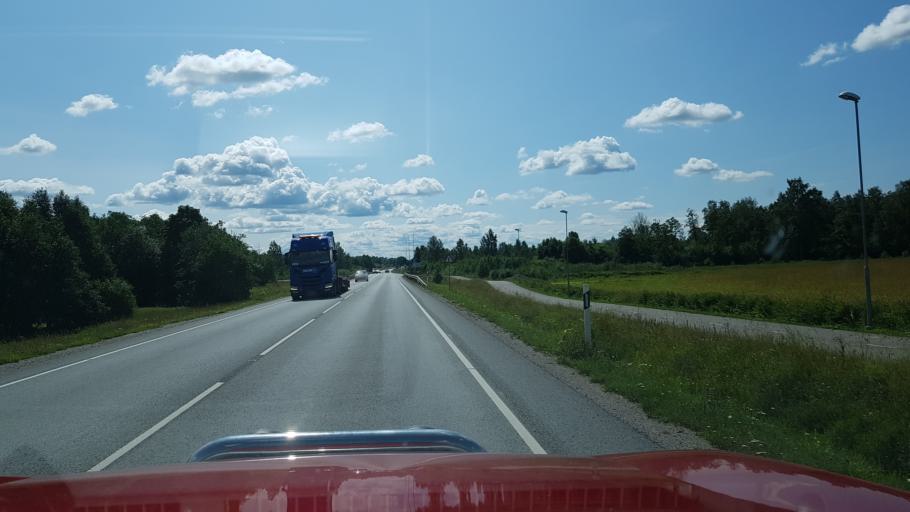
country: EE
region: Laeaene-Virumaa
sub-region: Rakvere linn
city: Rakvere
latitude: 59.3478
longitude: 26.3397
